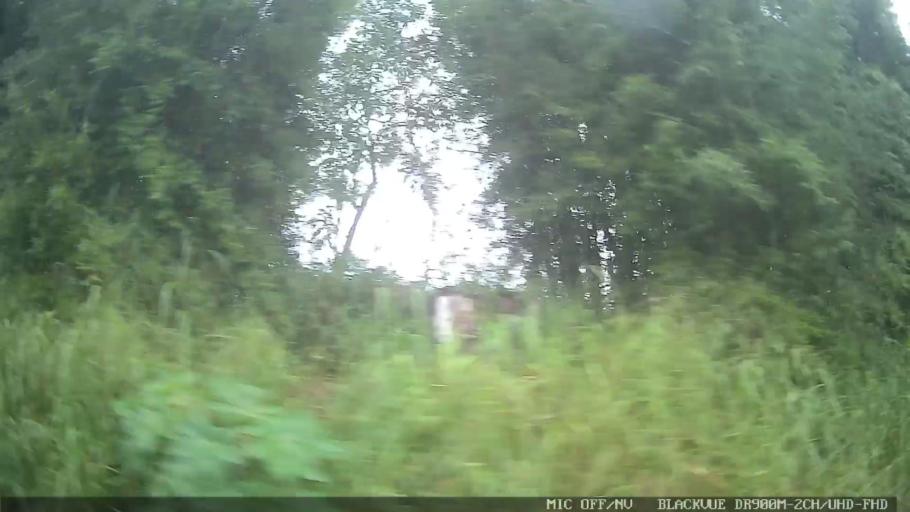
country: BR
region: Sao Paulo
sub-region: Suzano
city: Suzano
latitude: -23.6479
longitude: -46.2694
